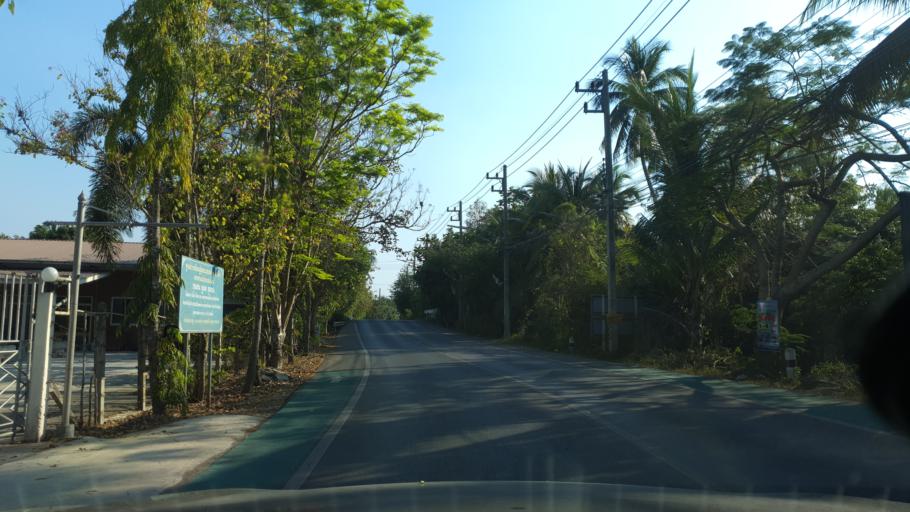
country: TH
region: Samut Songkhram
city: Bang Khon Thi
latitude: 13.4503
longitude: 99.9412
